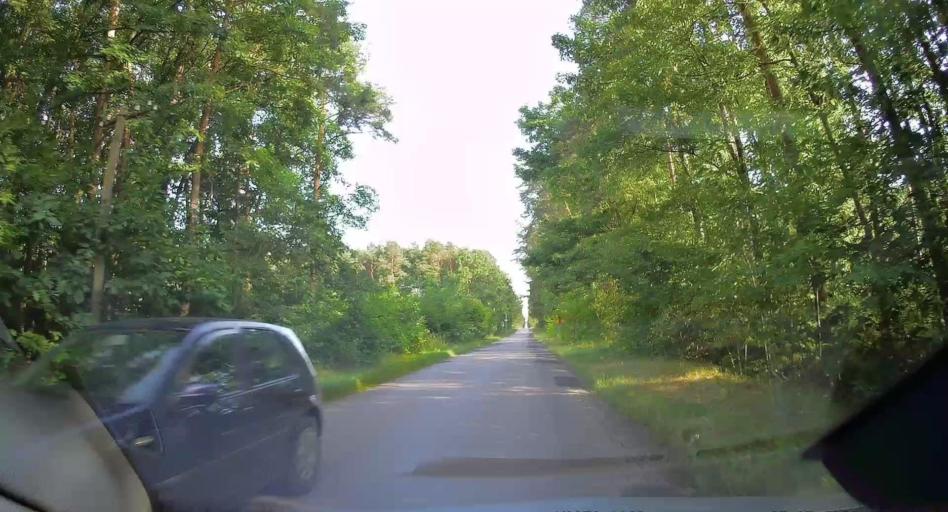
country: PL
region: Swietokrzyskie
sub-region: Powiat konecki
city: Konskie
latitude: 51.2264
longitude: 20.3846
